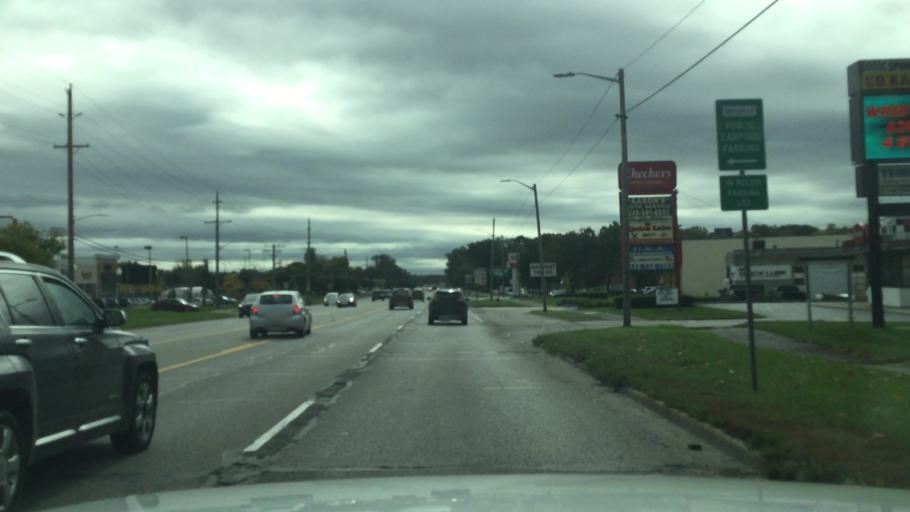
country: US
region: Michigan
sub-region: Oakland County
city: Keego Harbor
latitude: 42.6536
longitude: -83.3724
